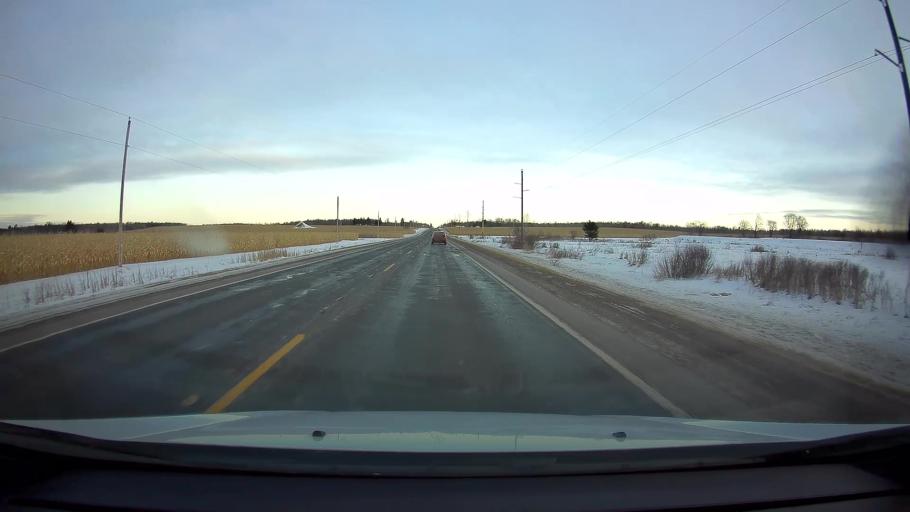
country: US
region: Wisconsin
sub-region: Barron County
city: Turtle Lake
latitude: 45.3451
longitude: -92.1674
